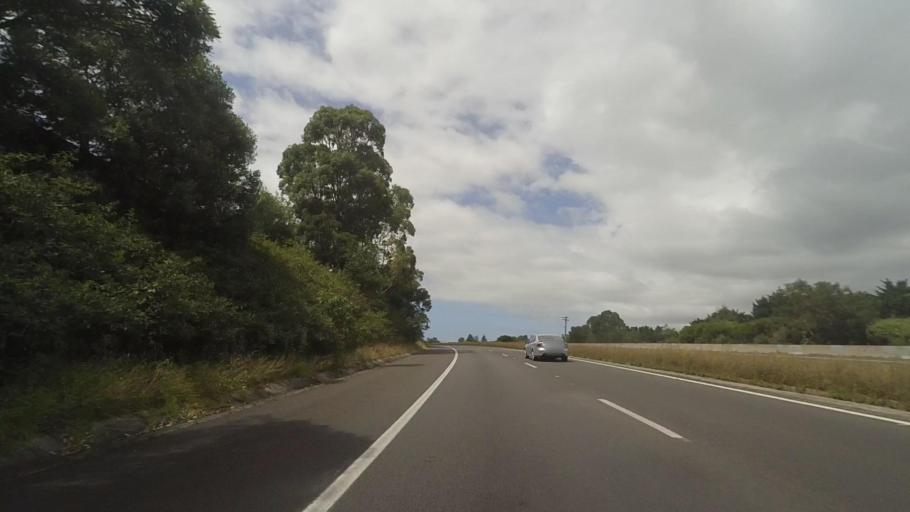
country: AU
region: New South Wales
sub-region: Kiama
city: Kiama
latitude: -34.6723
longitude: 150.8430
